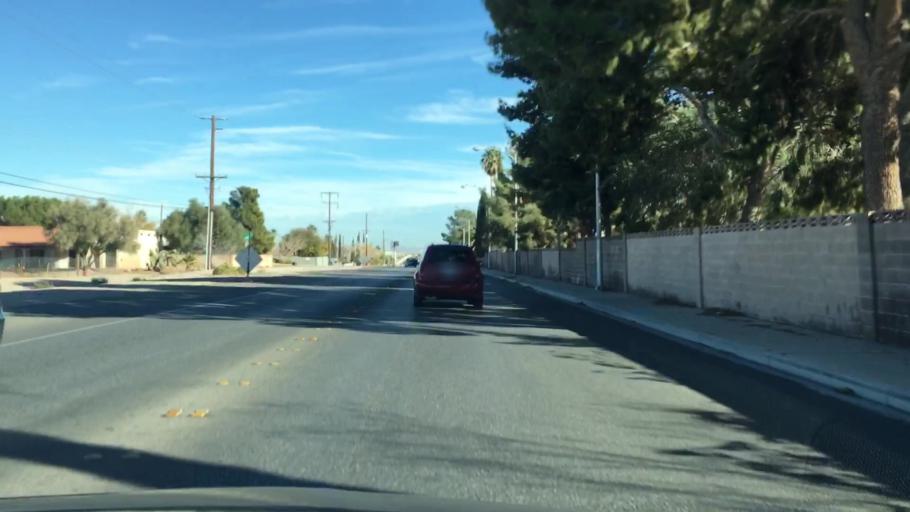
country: US
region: Nevada
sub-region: Clark County
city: Paradise
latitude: 36.0571
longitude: -115.1889
